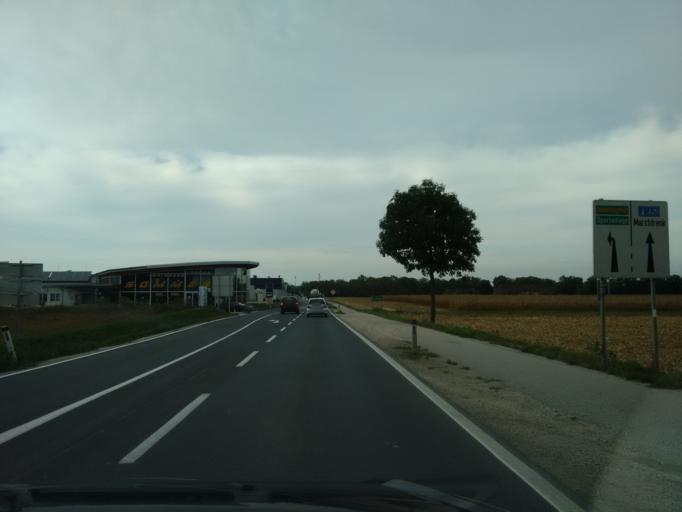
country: AT
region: Upper Austria
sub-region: Wels-Land
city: Marchtrenk
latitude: 48.1669
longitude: 14.1288
